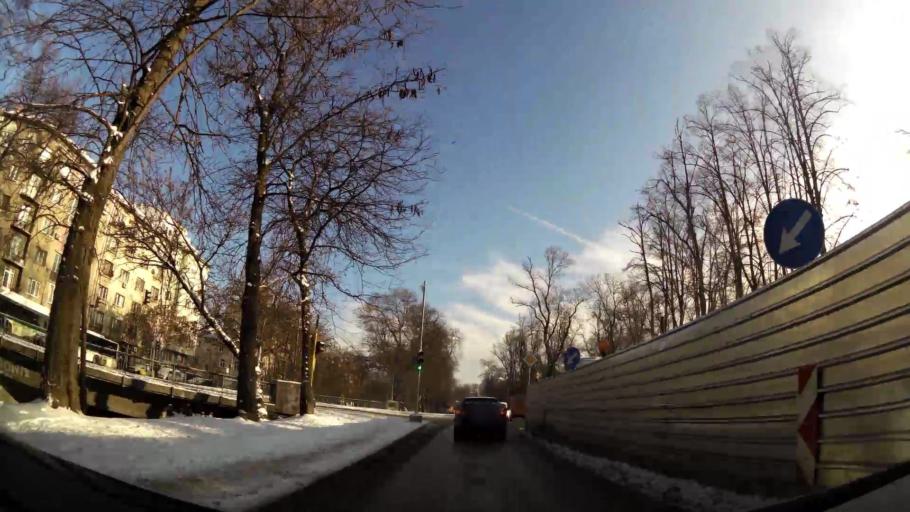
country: BG
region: Sofia-Capital
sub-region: Stolichna Obshtina
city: Sofia
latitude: 42.6922
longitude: 23.3442
